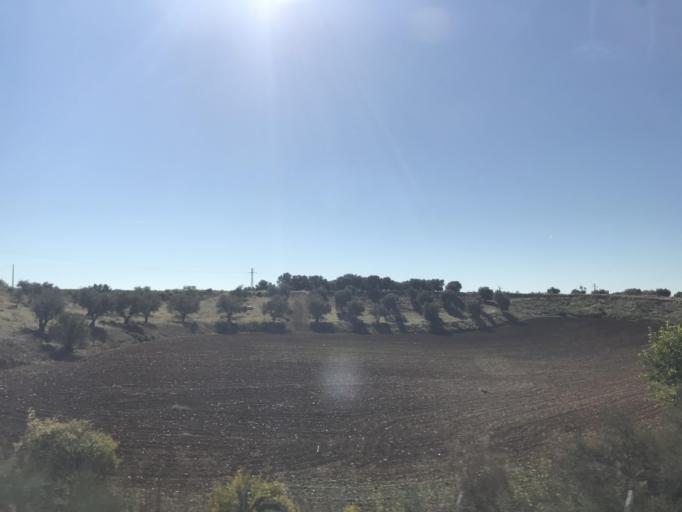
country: ES
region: Madrid
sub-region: Provincia de Madrid
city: Torres de la Alameda
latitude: 40.4275
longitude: -3.3774
